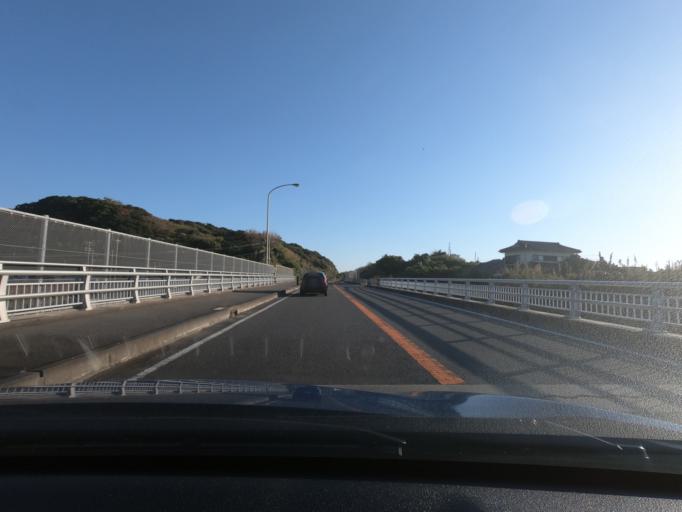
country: JP
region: Kagoshima
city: Akune
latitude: 31.9417
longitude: 130.2169
